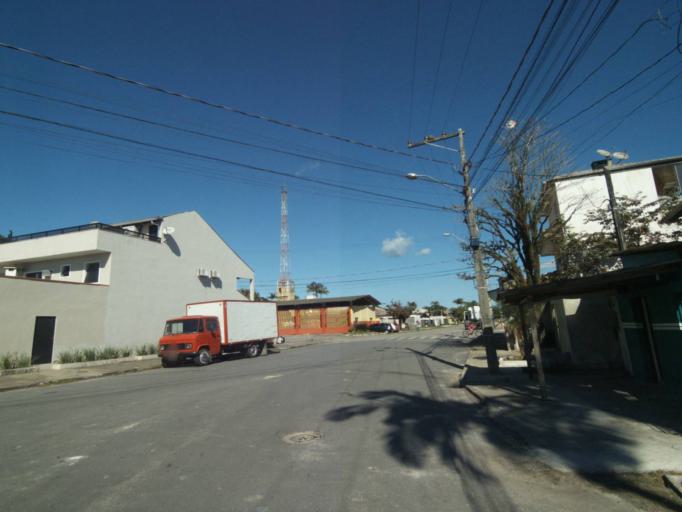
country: BR
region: Parana
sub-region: Paranagua
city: Paranagua
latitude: -25.5131
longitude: -48.4999
